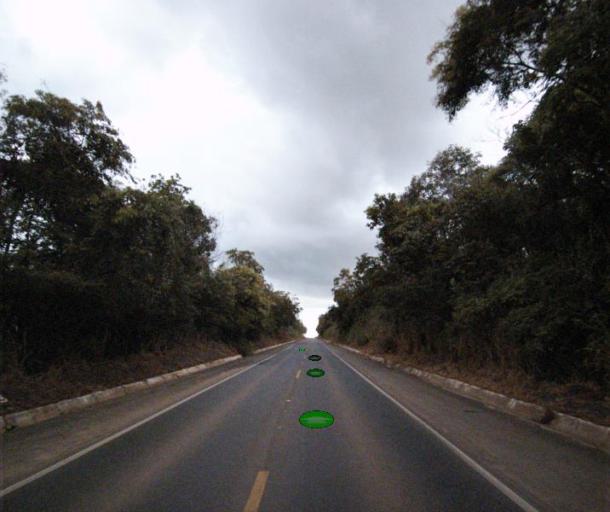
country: BR
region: Goias
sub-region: Uruacu
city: Uruacu
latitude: -14.6890
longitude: -49.2112
